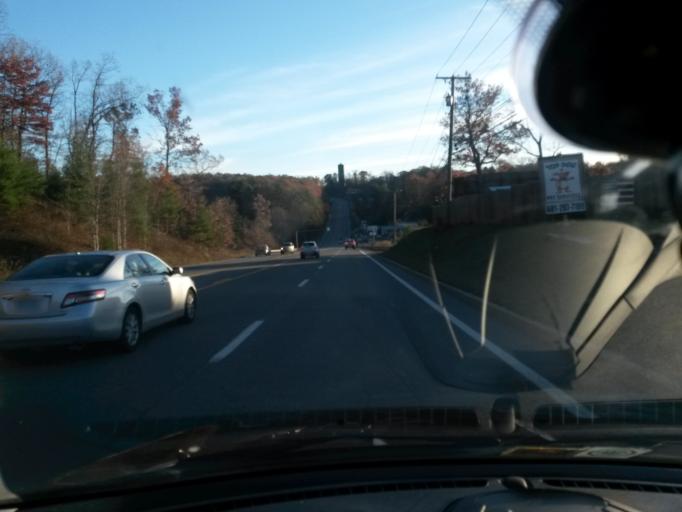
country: US
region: West Virginia
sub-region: Raleigh County
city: Prosperity
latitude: 37.8352
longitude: -81.1946
